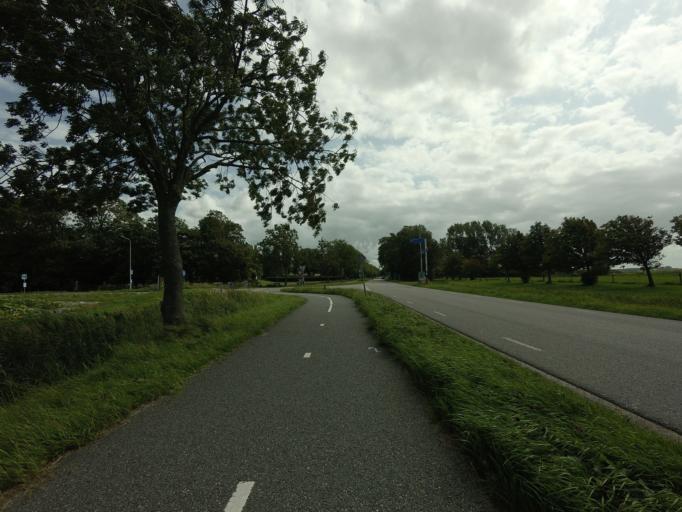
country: NL
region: Friesland
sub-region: Gemeente Harlingen
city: Harlingen
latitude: 53.1337
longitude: 5.4697
